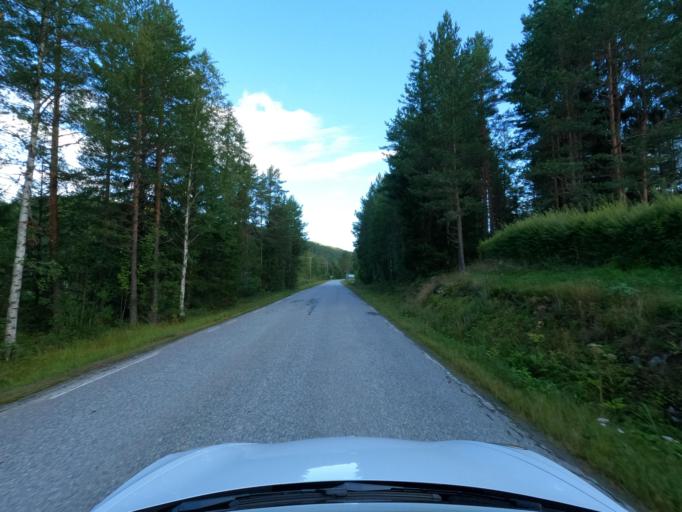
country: NO
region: Telemark
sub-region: Hjartdal
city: Sauland
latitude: 59.8237
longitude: 9.0648
